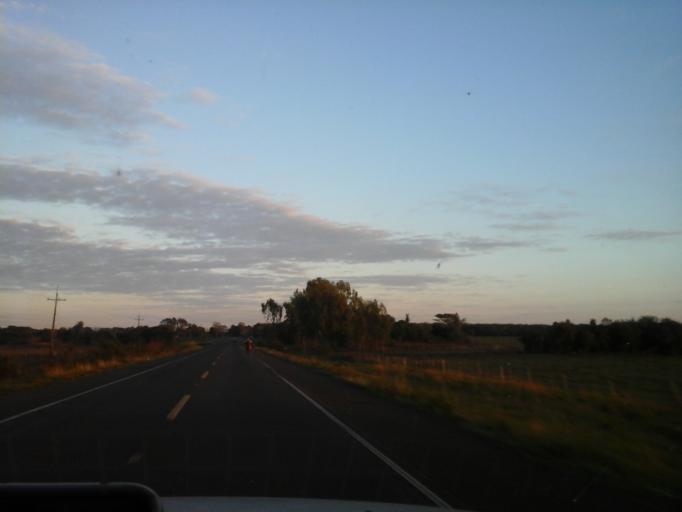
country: PY
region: Itapua
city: General Delgado
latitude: -27.0785
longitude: -56.5705
